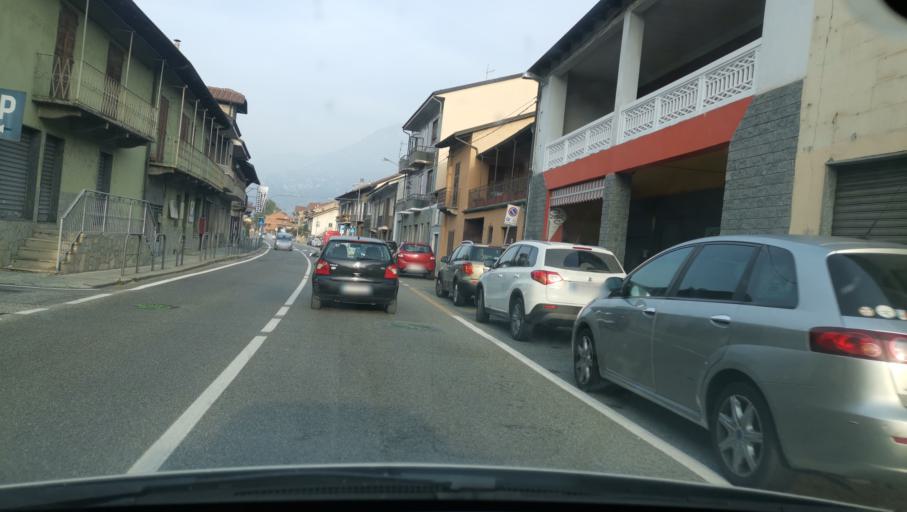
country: IT
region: Piedmont
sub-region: Provincia di Torino
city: Borgone Susa
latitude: 45.1223
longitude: 7.2374
